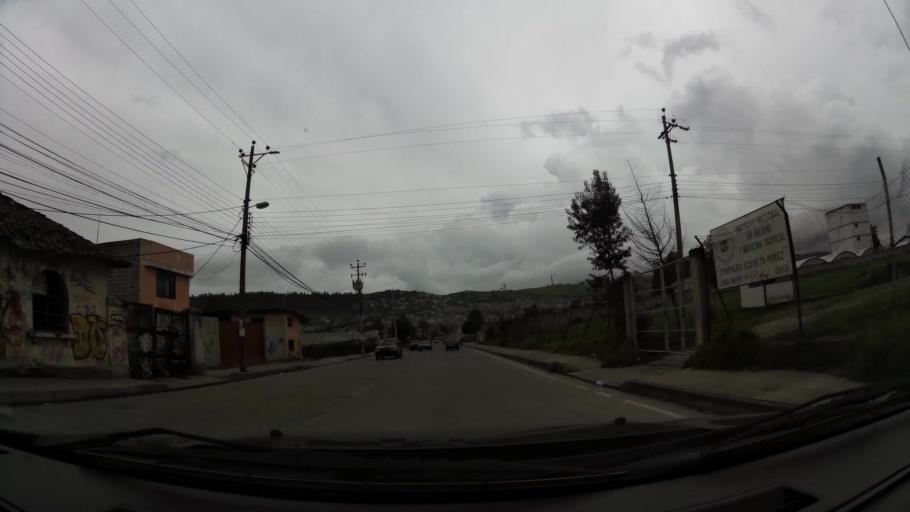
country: EC
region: Pichincha
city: Quito
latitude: -0.3183
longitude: -78.5432
